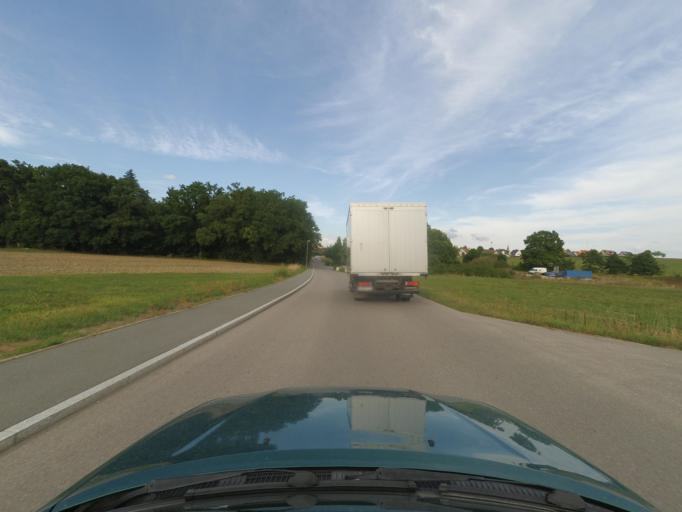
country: DE
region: Bavaria
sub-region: Regierungsbezirk Mittelfranken
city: Burgthann
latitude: 49.3259
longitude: 11.3188
